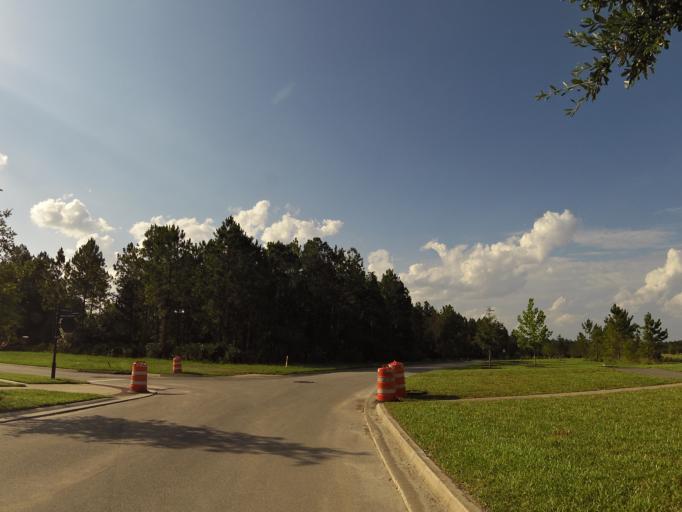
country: US
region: Florida
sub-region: Clay County
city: Green Cove Springs
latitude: 30.0284
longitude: -81.6351
